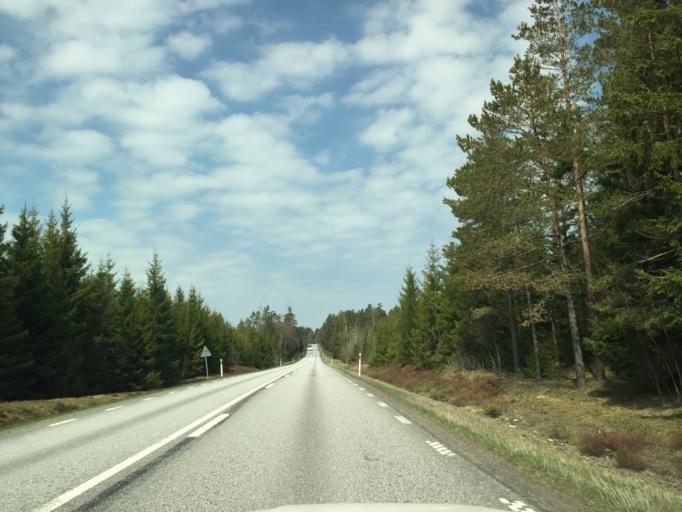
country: SE
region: Vaestra Goetaland
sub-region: Bengtsfors Kommun
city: Dals Langed
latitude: 58.8134
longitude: 12.1453
